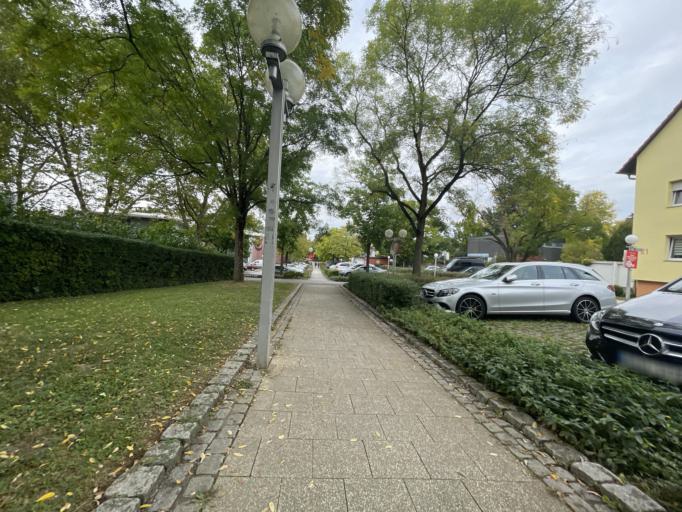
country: DE
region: Baden-Wuerttemberg
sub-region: Regierungsbezirk Stuttgart
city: Marbach am Neckar
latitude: 48.9337
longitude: 9.2575
